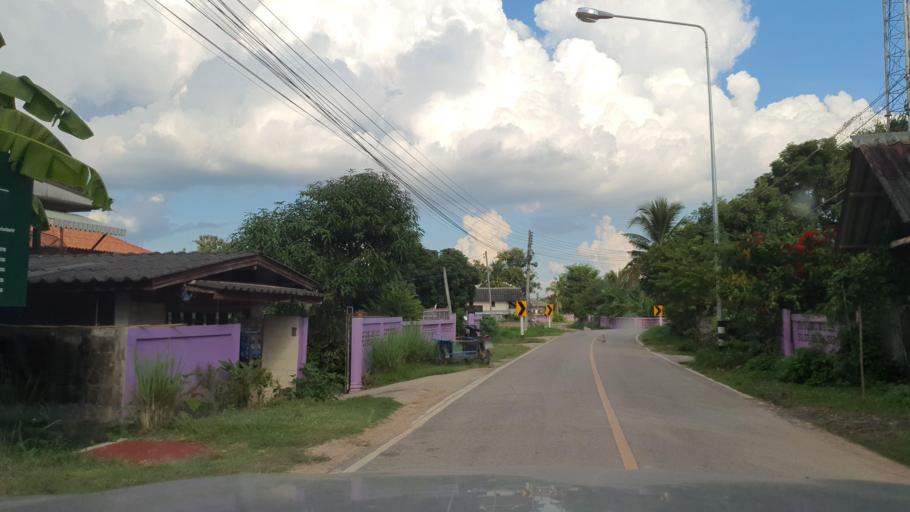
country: TH
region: Phayao
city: Phayao
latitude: 19.1801
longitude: 99.8432
